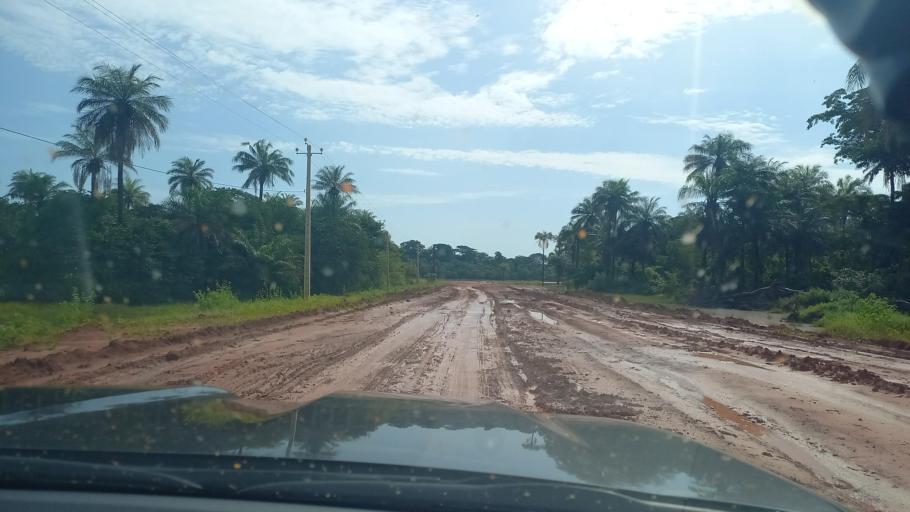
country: SN
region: Ziguinchor
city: Ziguinchor
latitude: 12.6734
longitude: -16.2055
